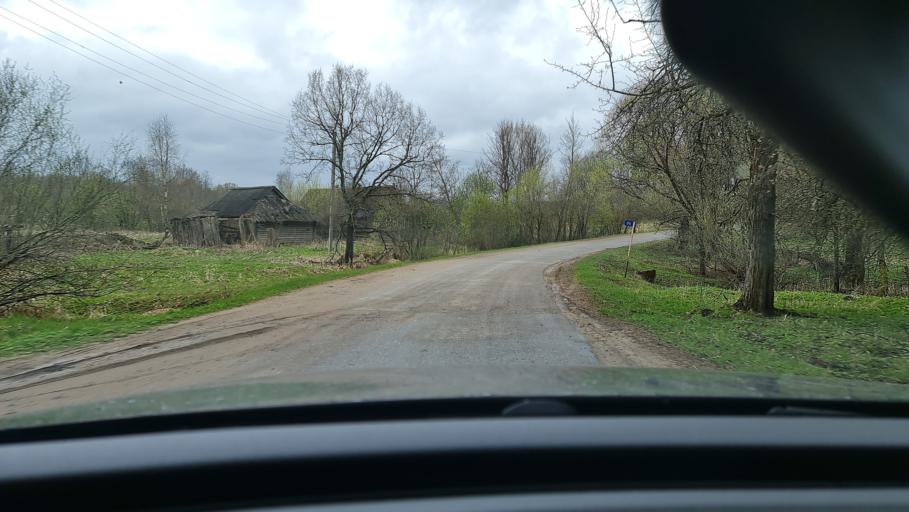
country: RU
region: Novgorod
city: Marevo
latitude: 57.1108
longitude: 31.7908
